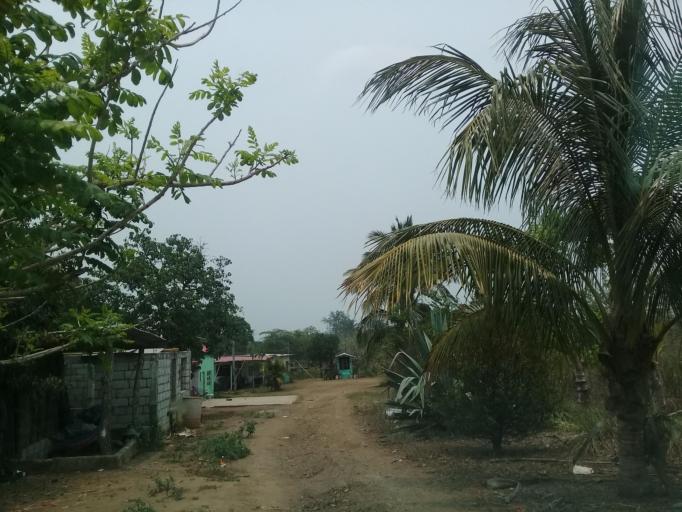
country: MX
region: Veracruz
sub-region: Medellin
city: La Laguna y Monte del Castillo
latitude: 18.9723
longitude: -96.1388
